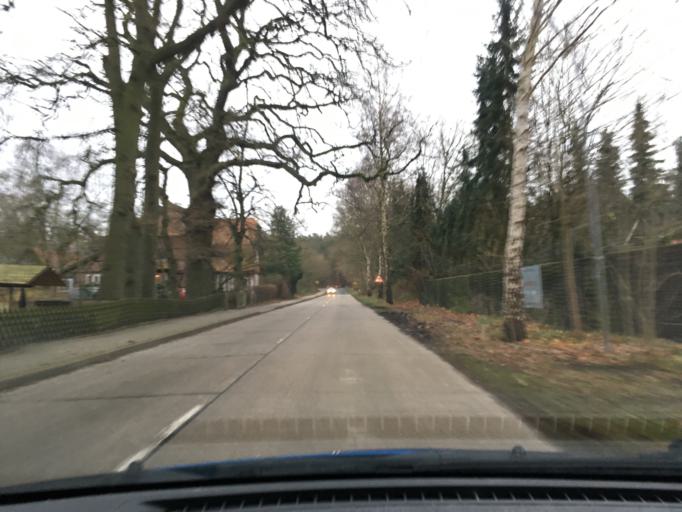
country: DE
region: Lower Saxony
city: Bleckede
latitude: 53.2805
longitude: 10.7573
